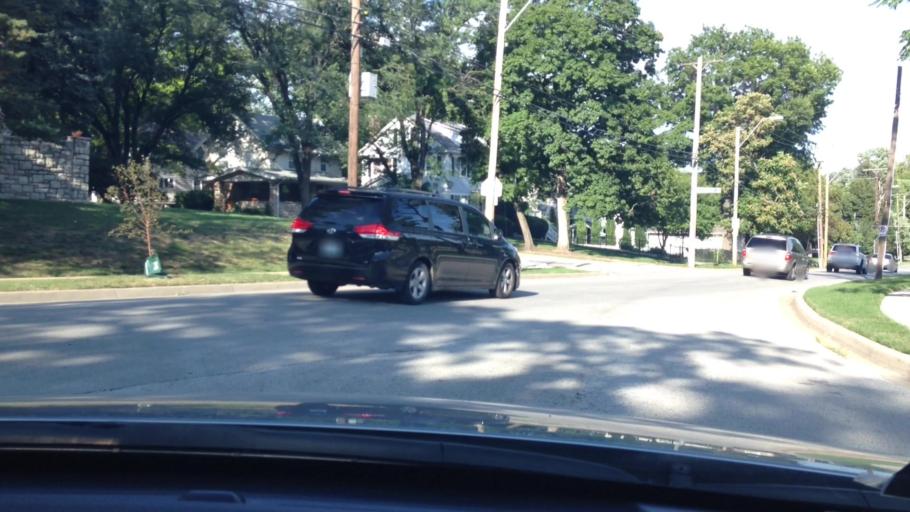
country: US
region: Kansas
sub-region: Johnson County
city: Mission Hills
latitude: 39.0277
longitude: -94.5895
